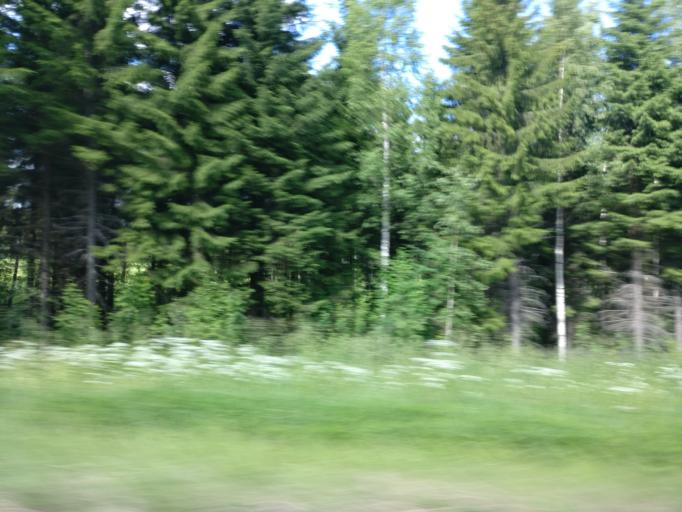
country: FI
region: Southern Savonia
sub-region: Savonlinna
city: Kerimaeki
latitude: 61.8411
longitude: 29.2107
